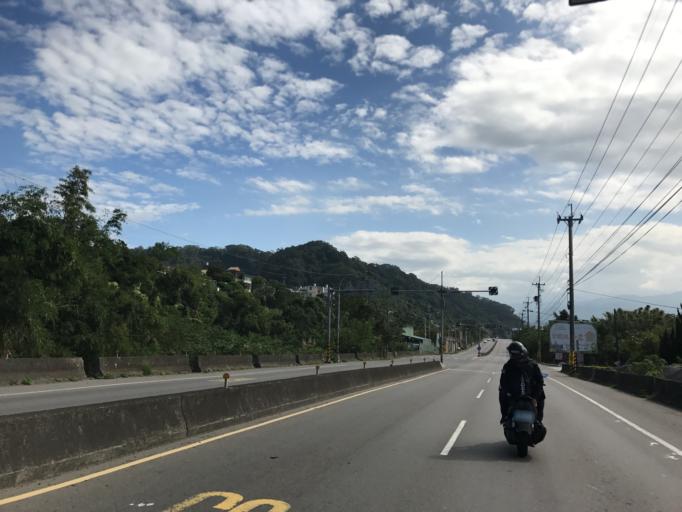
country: TW
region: Taiwan
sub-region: Hsinchu
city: Zhubei
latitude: 24.7460
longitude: 121.1015
